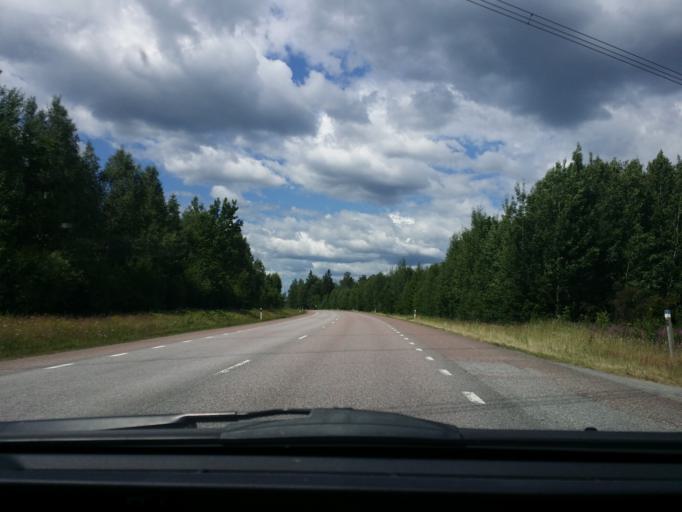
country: SE
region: OErebro
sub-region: Orebro Kommun
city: Hovsta
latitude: 59.4322
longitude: 15.1662
